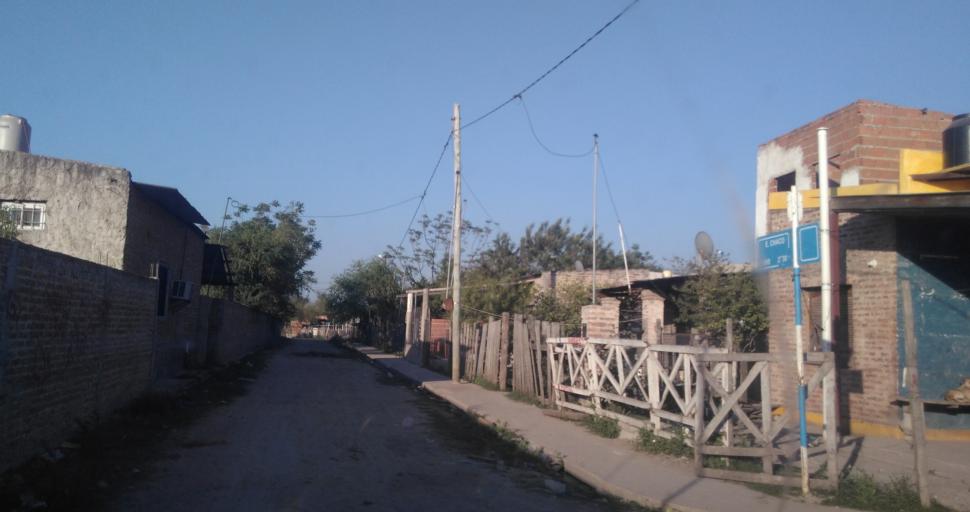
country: AR
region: Chaco
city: Resistencia
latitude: -27.4835
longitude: -58.9955
